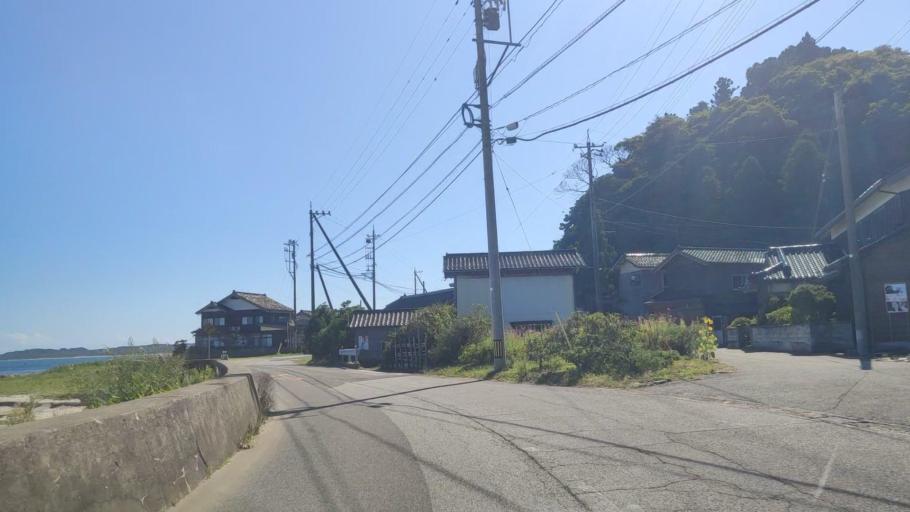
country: JP
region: Toyama
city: Nyuzen
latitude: 37.4910
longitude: 137.3422
